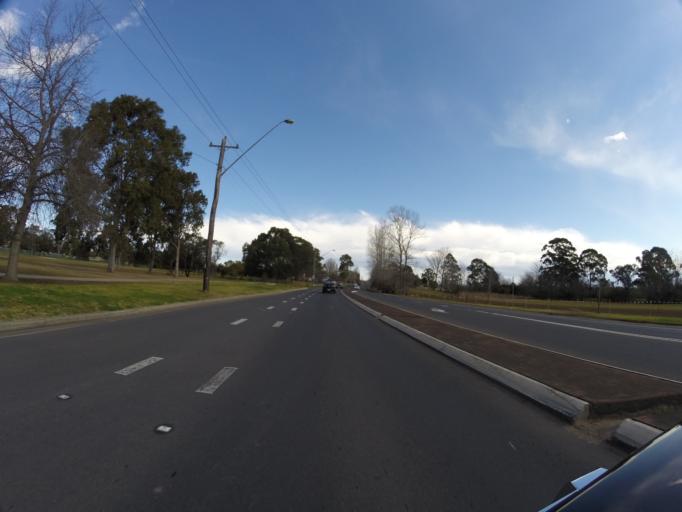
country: AU
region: New South Wales
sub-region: Camden
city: Elderslie
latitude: -34.0499
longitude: 150.7140
